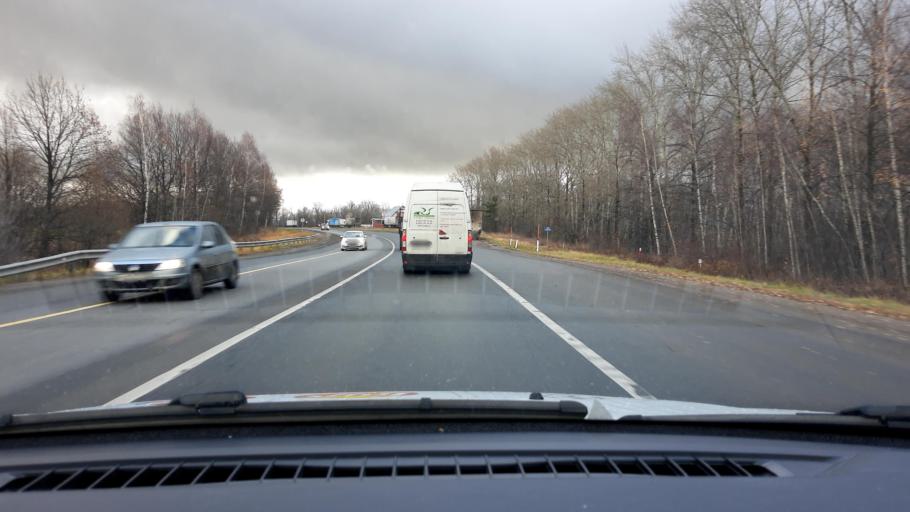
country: RU
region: Nizjnij Novgorod
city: Pamyat' Parizhskoy Kommuny
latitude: 55.9979
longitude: 44.6403
